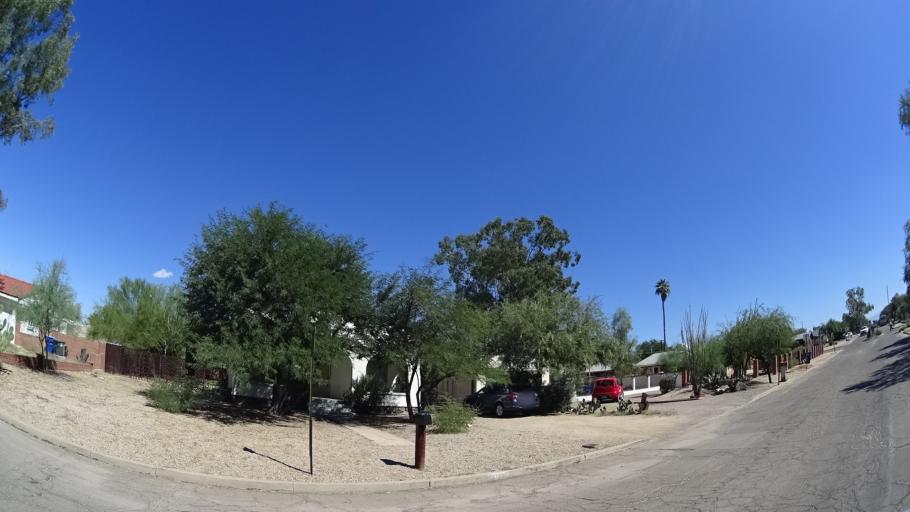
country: US
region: Arizona
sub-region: Pima County
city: Tucson
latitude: 32.2437
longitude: -110.9521
